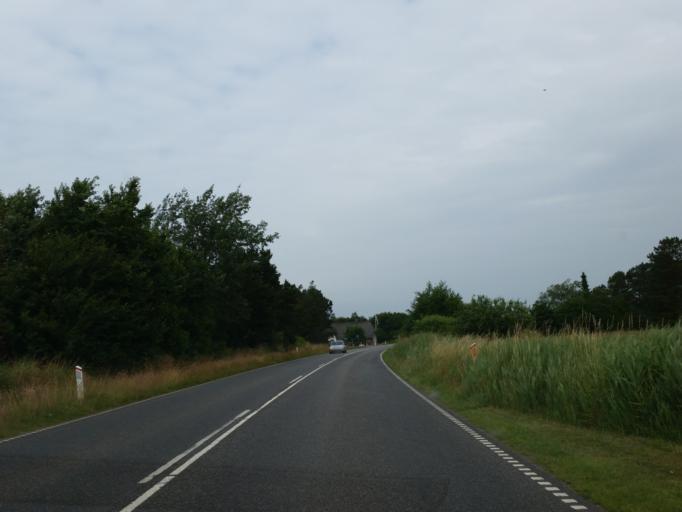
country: DE
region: Schleswig-Holstein
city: List
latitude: 55.1403
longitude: 8.5471
